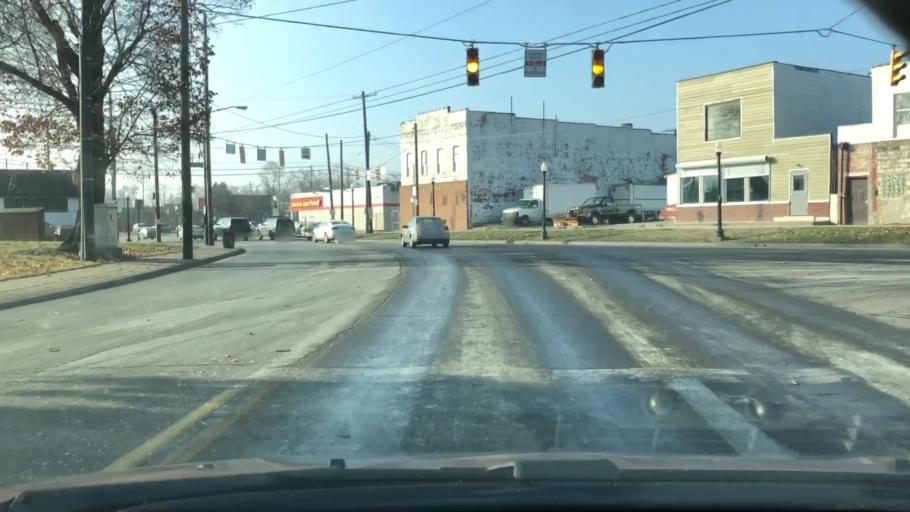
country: US
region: Ohio
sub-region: Franklin County
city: Bexley
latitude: 40.0213
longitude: -82.9647
